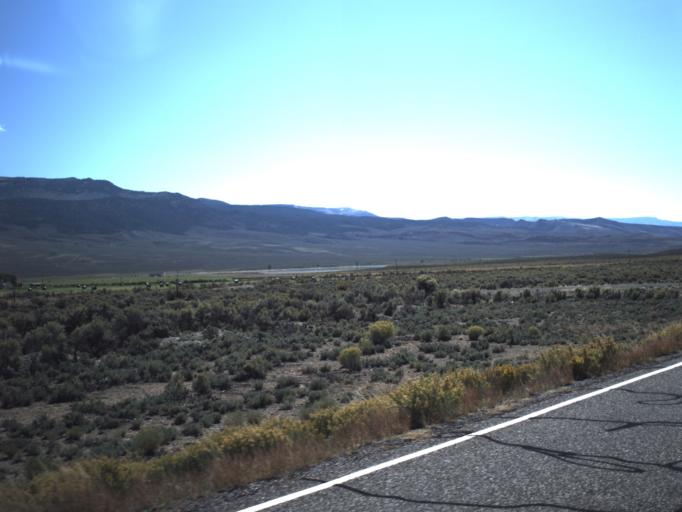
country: US
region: Utah
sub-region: Piute County
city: Junction
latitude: 38.2496
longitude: -111.9871
